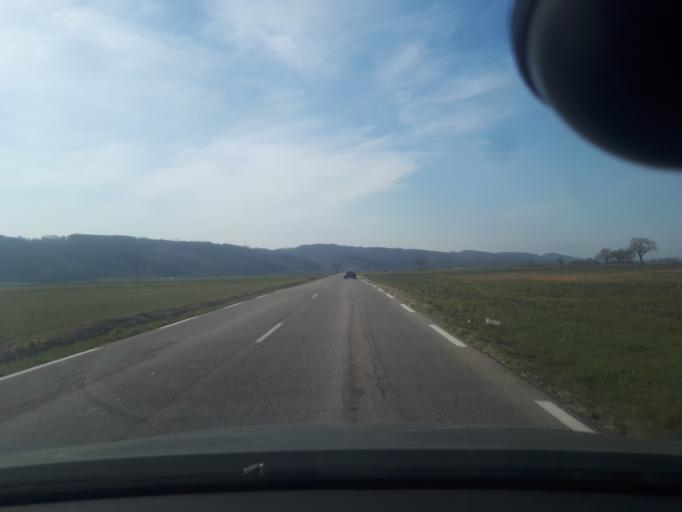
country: FR
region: Rhone-Alpes
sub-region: Departement de l'Isere
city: Champier
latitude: 45.4286
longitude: 5.2758
